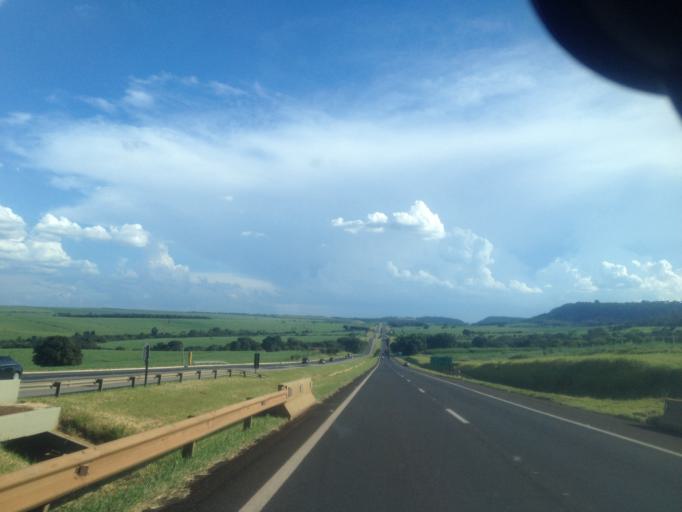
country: BR
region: Sao Paulo
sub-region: Sao Simao
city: Sao Simao
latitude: -21.4798
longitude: -47.6406
